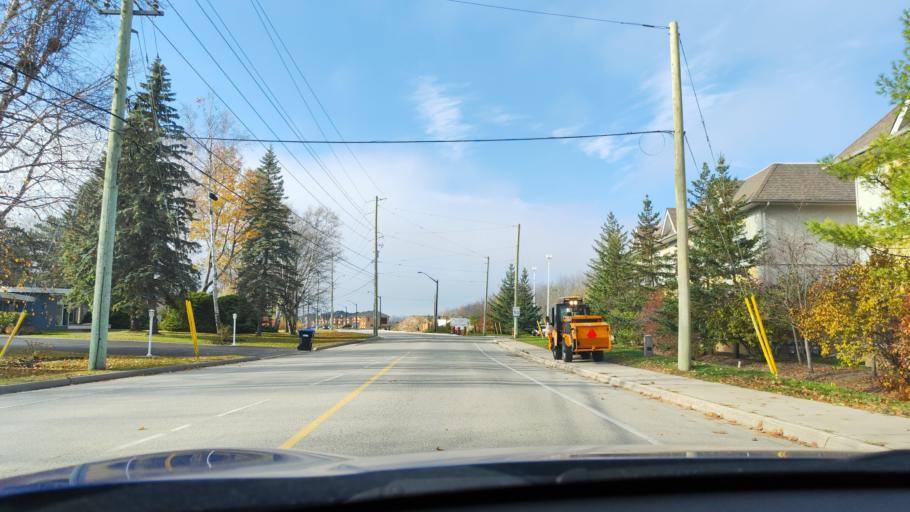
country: CA
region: Ontario
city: Wasaga Beach
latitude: 44.4683
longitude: -80.0754
